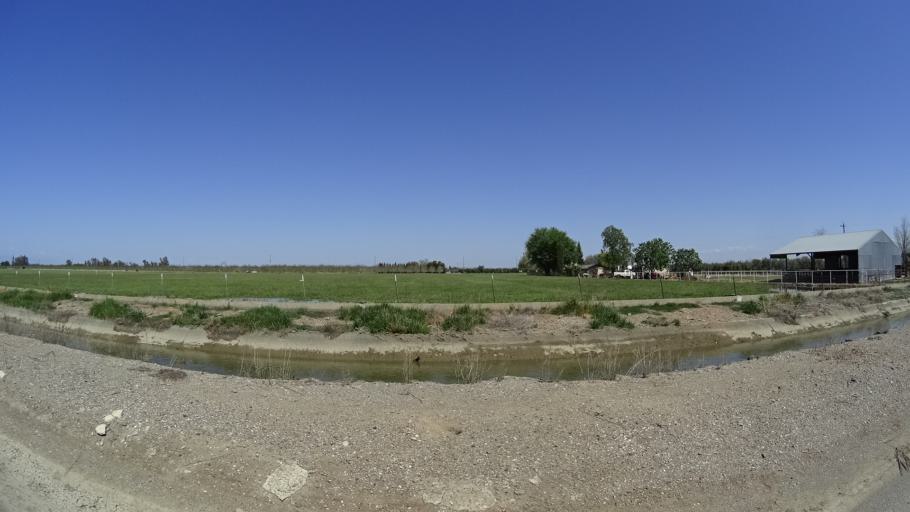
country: US
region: California
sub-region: Glenn County
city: Orland
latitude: 39.7652
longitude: -122.1694
